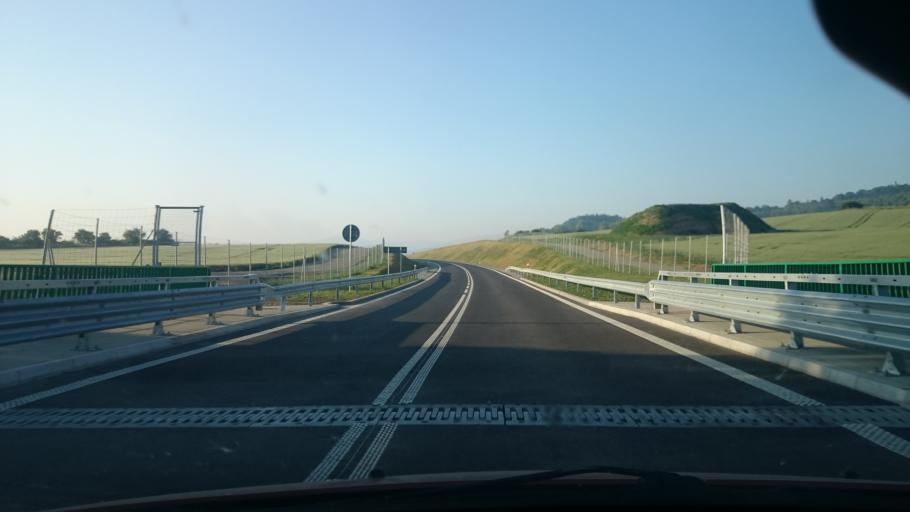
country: PL
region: Lower Silesian Voivodeship
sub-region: Powiat klodzki
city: Klodzko
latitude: 50.4128
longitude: 16.6272
